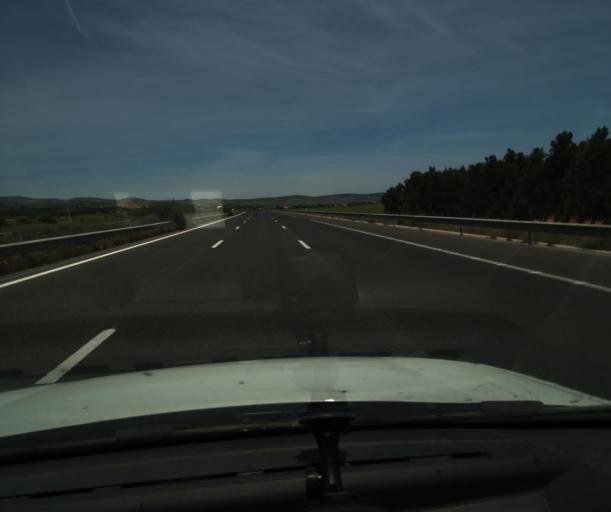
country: FR
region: Languedoc-Roussillon
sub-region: Departement des Pyrenees-Orientales
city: Salses-le-Chateau
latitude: 42.8170
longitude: 2.9075
